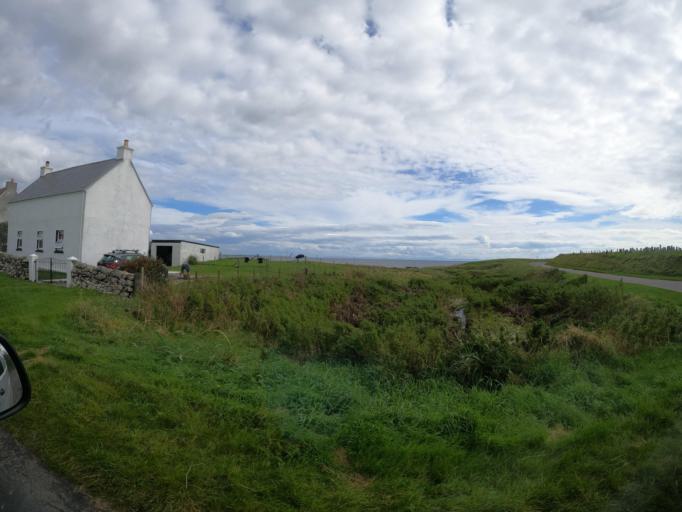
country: GB
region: Scotland
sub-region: Eilean Siar
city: Barra
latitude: 56.4705
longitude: -6.8994
